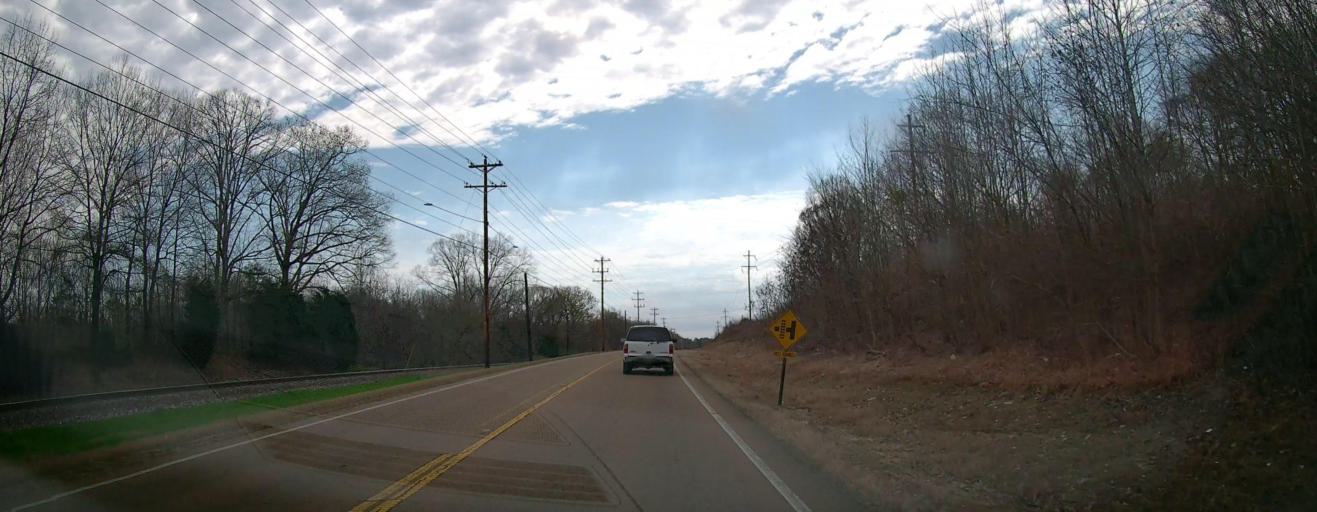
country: US
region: Mississippi
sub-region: Marshall County
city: Byhalia
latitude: 34.9016
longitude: -89.7445
